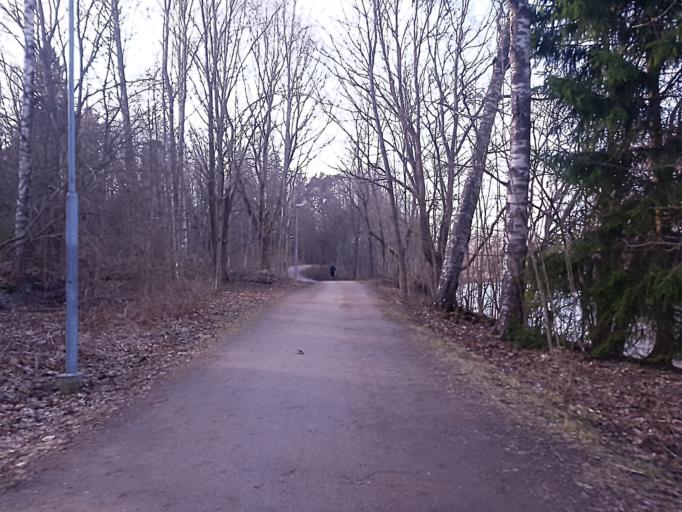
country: FI
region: Uusimaa
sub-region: Helsinki
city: Helsinki
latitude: 60.2408
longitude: 24.9728
